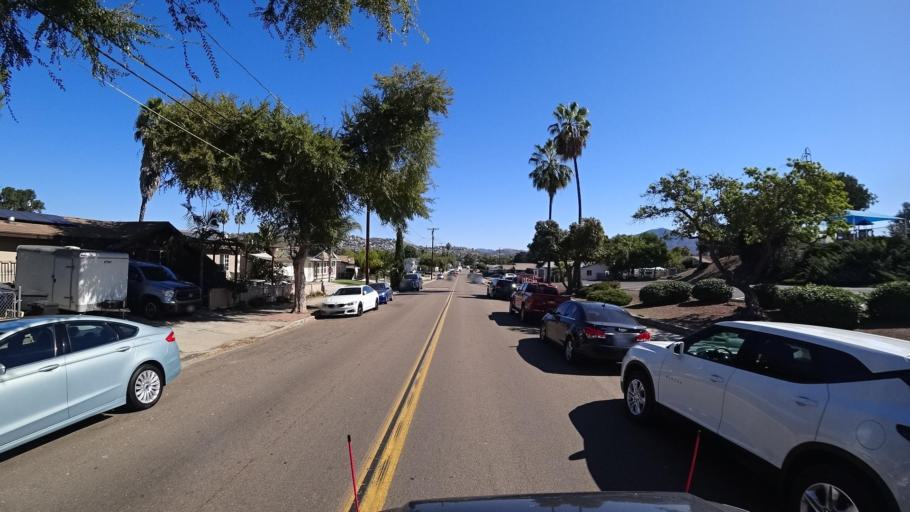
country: US
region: California
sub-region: San Diego County
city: La Presa
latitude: 32.7053
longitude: -117.0153
